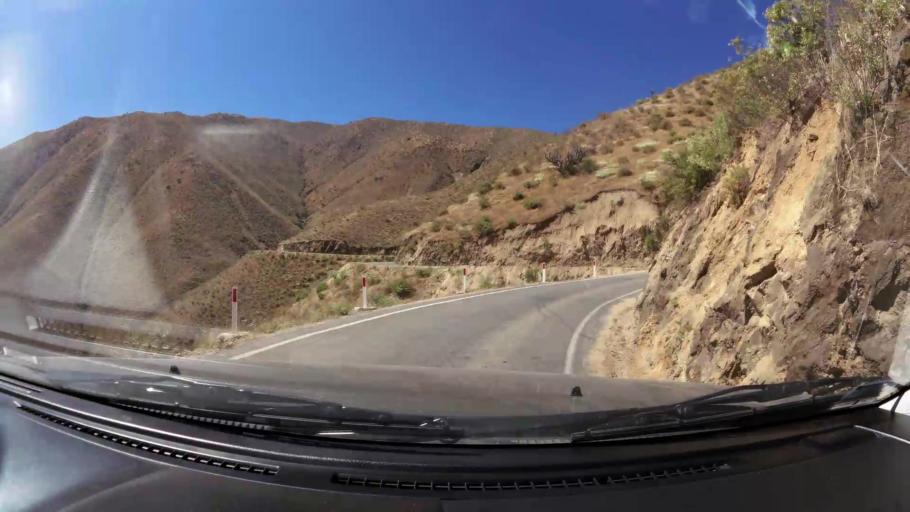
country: PE
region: Ica
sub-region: Provincia de Pisco
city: Huancano
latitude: -13.7231
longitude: -75.4553
